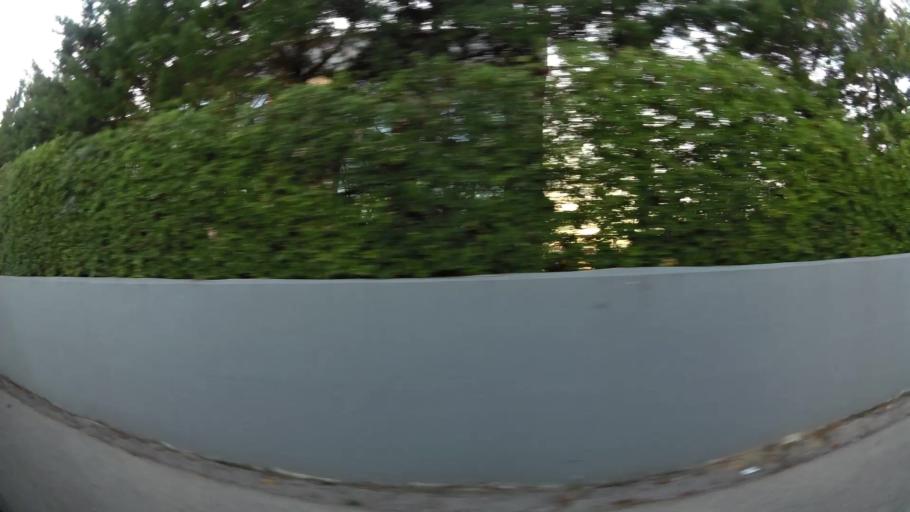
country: GR
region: Attica
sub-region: Nomarchia Anatolikis Attikis
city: Kryoneri
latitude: 38.1431
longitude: 23.8421
